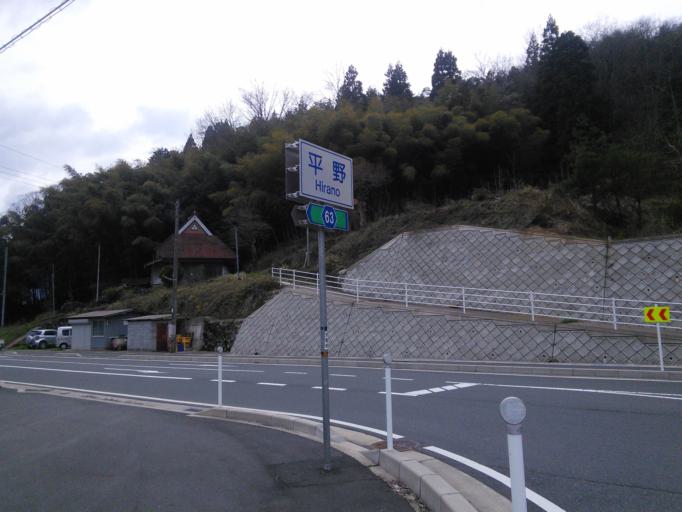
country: JP
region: Kyoto
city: Fukuchiyama
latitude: 35.3492
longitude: 134.9451
